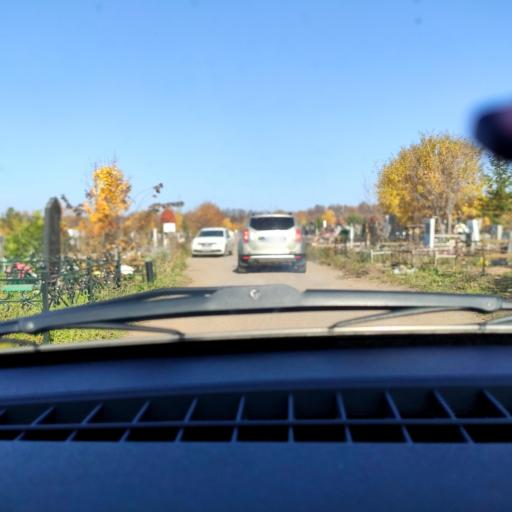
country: RU
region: Bashkortostan
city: Mikhaylovka
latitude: 54.8153
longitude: 55.8665
